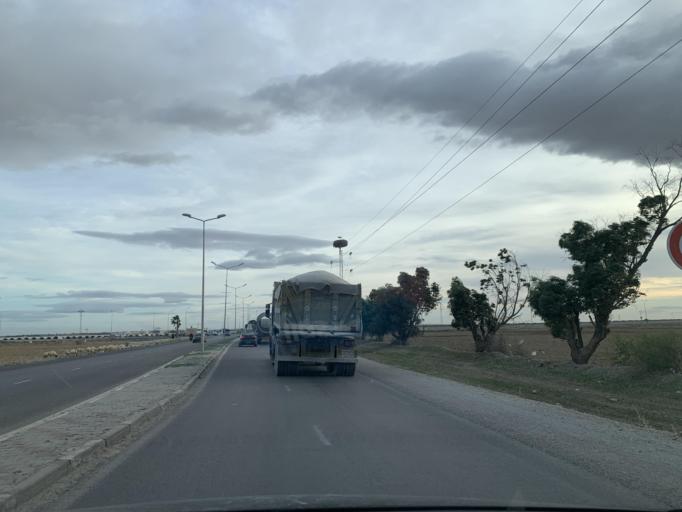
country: TN
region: Susah
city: Harqalah
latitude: 36.1039
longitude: 10.3881
